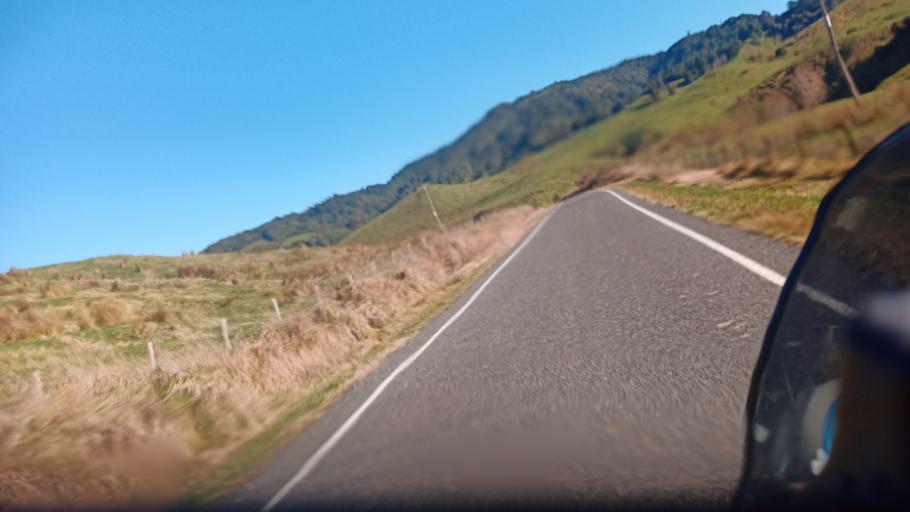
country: NZ
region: Gisborne
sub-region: Gisborne District
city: Gisborne
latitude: -38.5835
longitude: 177.5433
